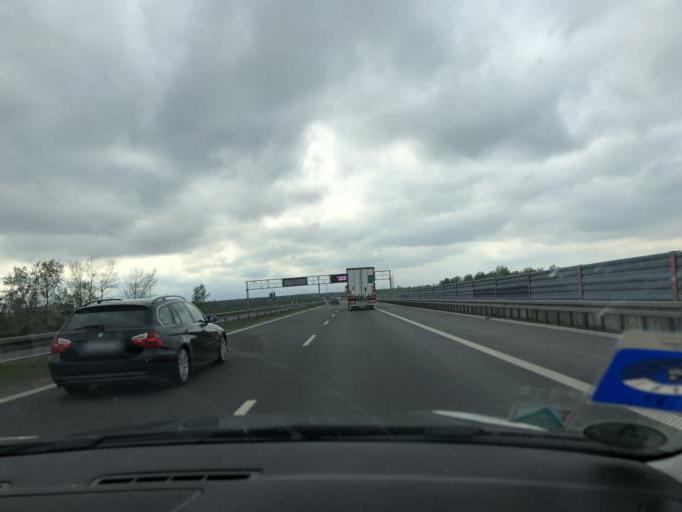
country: PL
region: Opole Voivodeship
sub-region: Powiat krapkowicki
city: Krapkowice
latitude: 50.5251
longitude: 17.9318
